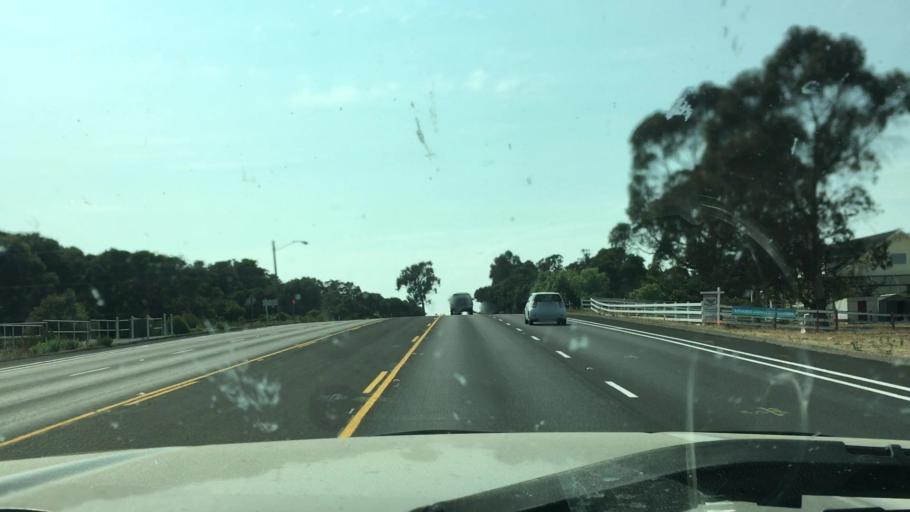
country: US
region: California
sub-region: San Luis Obispo County
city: Los Osos
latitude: 35.3071
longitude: -120.8153
